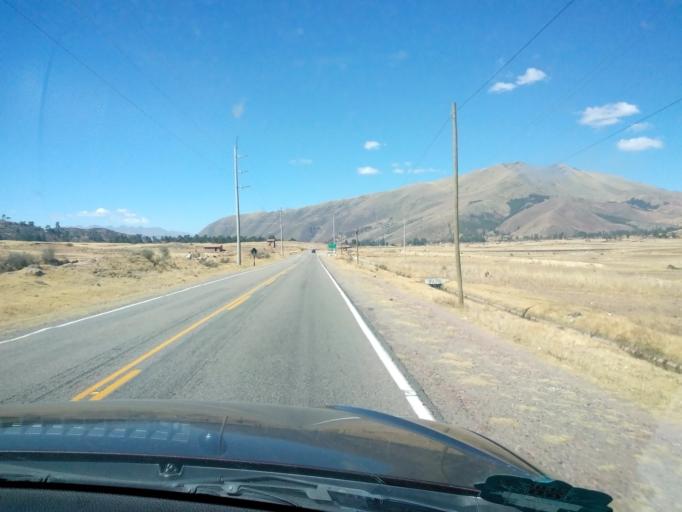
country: PE
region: Cusco
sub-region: Provincia de Canchis
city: Queromarca
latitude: -14.1615
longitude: -71.3866
